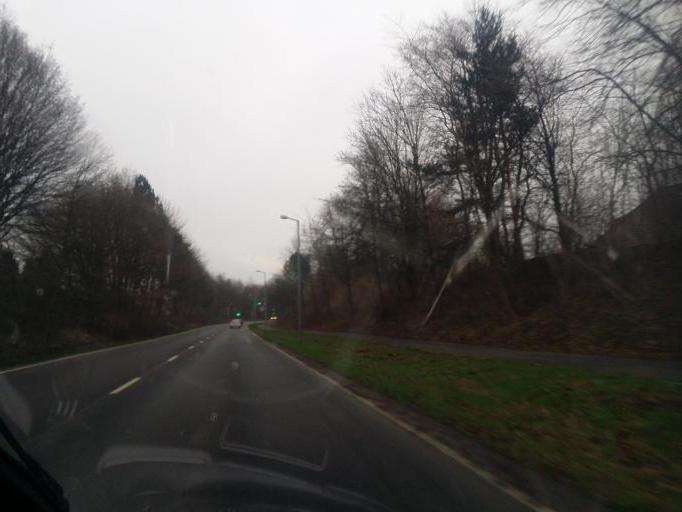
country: DE
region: Schleswig-Holstein
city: Heide
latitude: 54.2029
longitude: 9.1199
